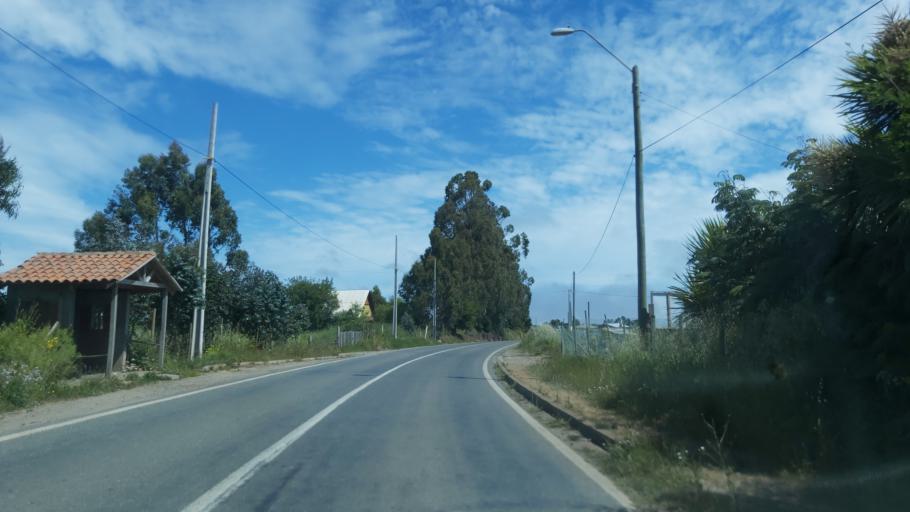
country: CL
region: Maule
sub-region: Provincia de Talca
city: Constitucion
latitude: -35.5790
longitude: -72.6012
